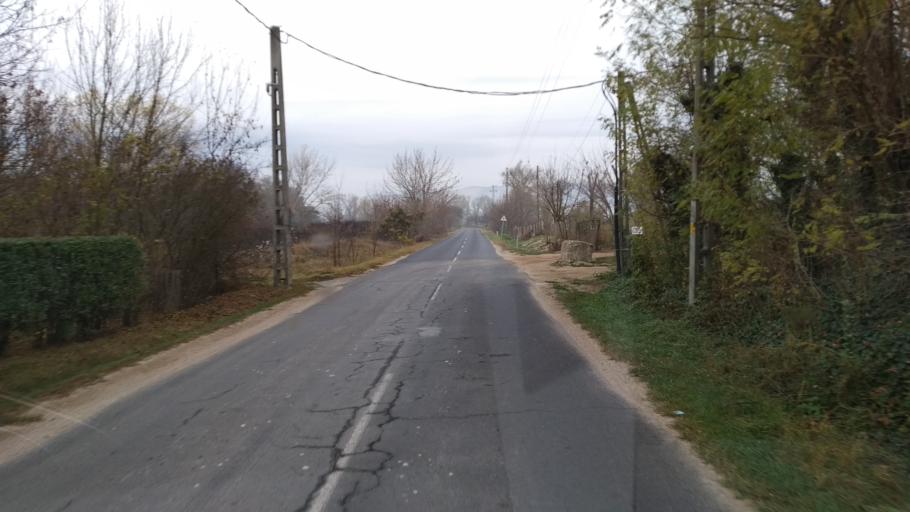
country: HU
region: Pest
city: Tahitotfalu
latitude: 47.7756
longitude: 19.0910
